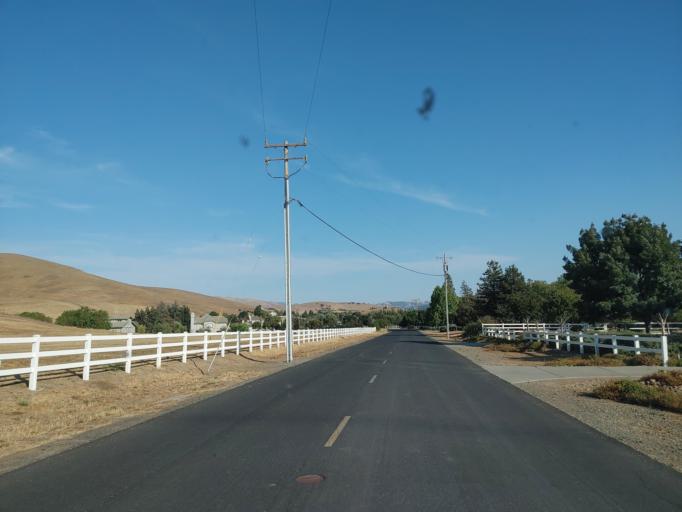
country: US
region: California
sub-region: San Benito County
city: Ridgemark
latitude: 36.8013
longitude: -121.3285
